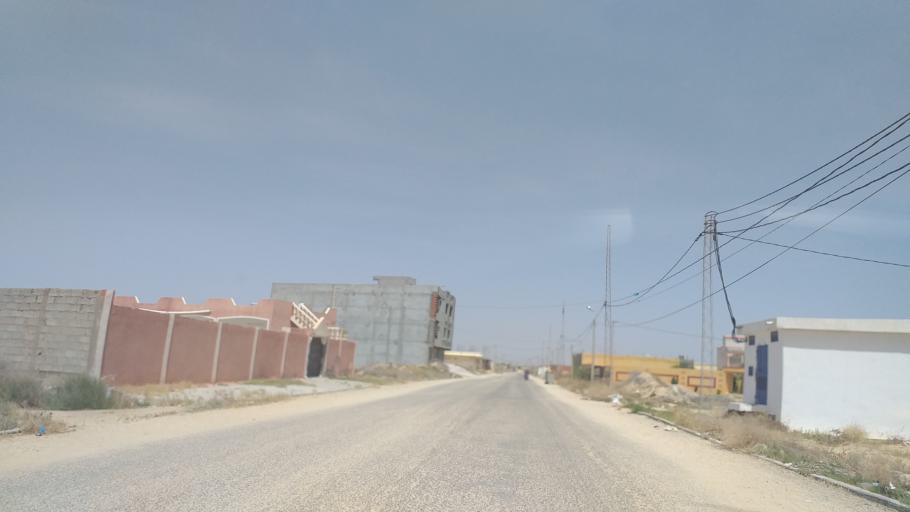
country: TN
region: Qabis
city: Gabes
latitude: 33.9534
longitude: 10.0670
